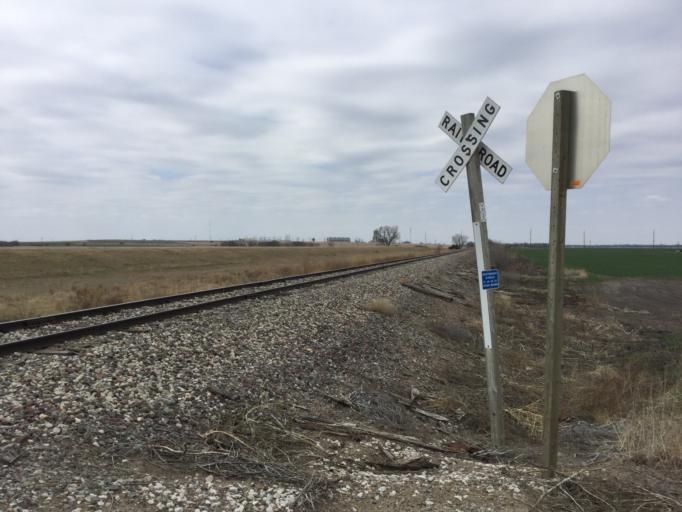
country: US
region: Kansas
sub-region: Barton County
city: Great Bend
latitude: 38.4008
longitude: -98.8483
